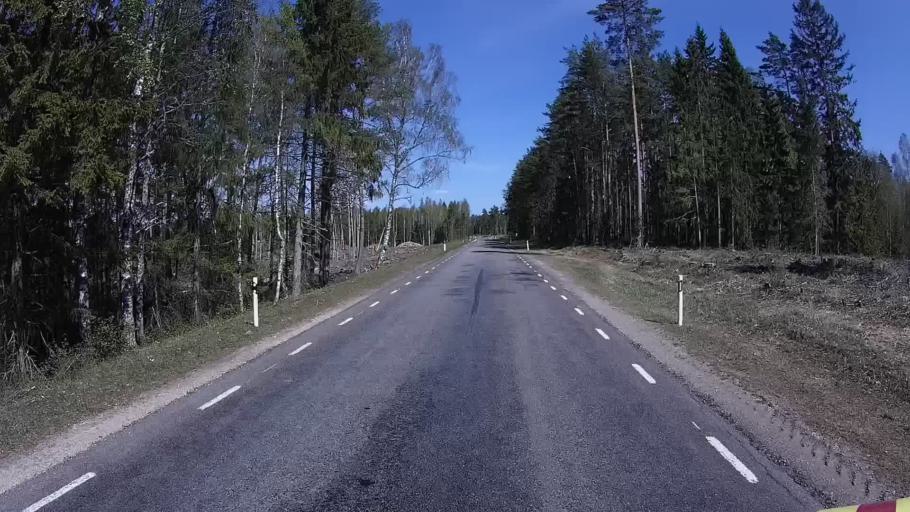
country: EE
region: Harju
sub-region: Nissi vald
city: Turba
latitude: 59.1155
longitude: 24.0550
